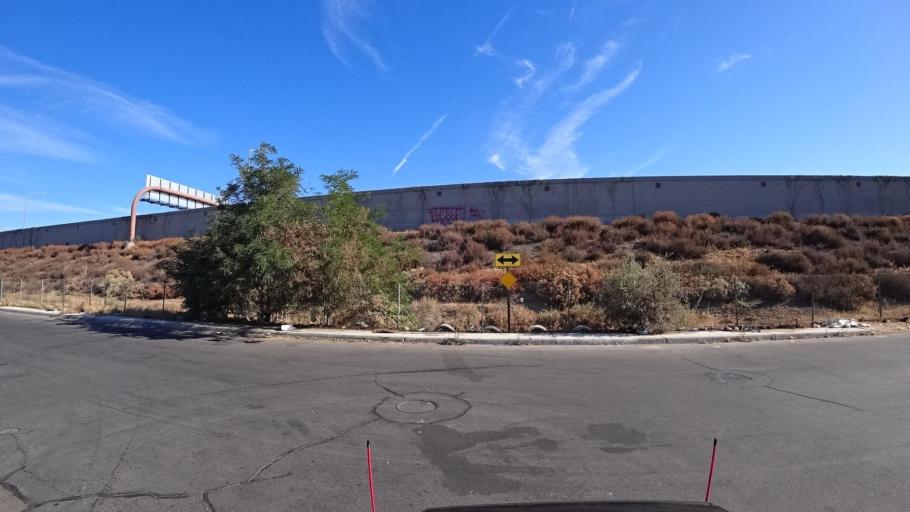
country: US
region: California
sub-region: Fresno County
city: Fresno
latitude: 36.7540
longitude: -119.7680
